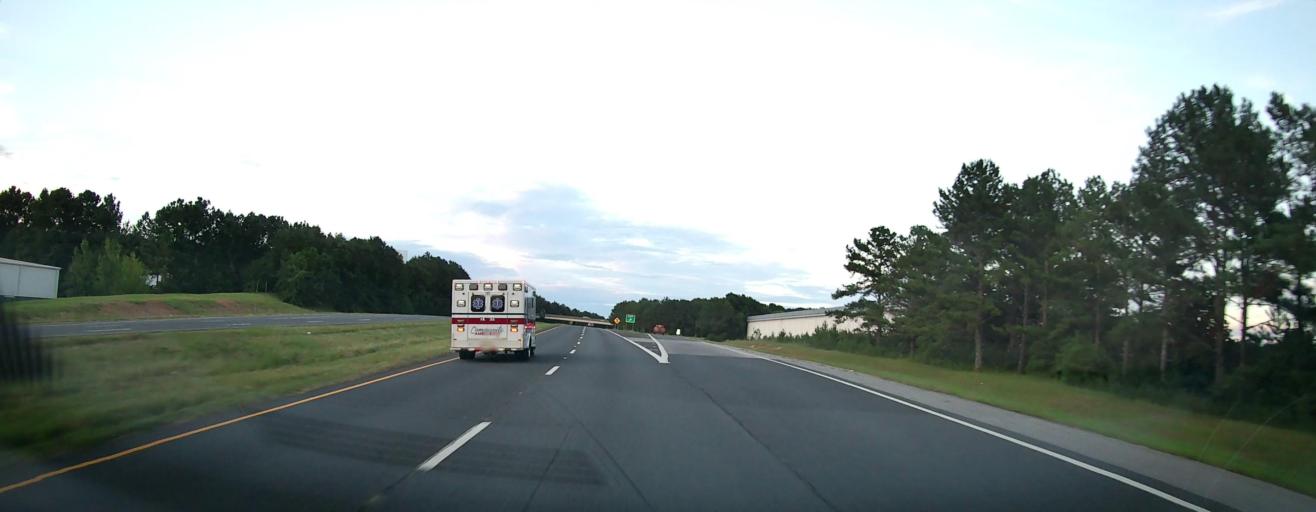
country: US
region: Georgia
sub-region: Muscogee County
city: Columbus
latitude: 32.5158
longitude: -84.9187
